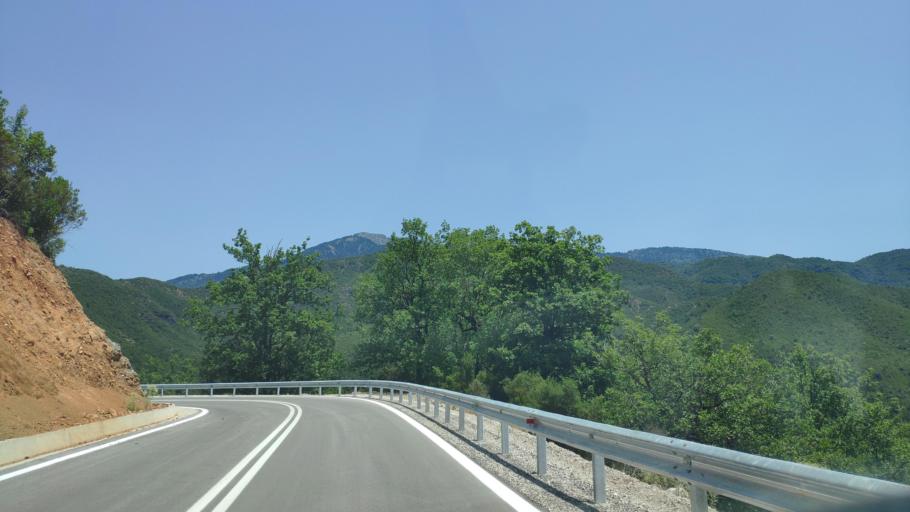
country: GR
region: Epirus
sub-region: Nomos Artas
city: Ano Kalentini
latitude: 39.1846
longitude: 21.3577
